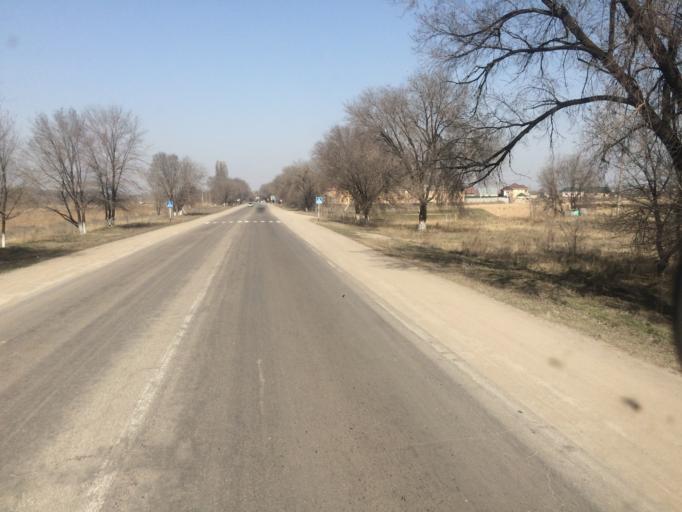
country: KZ
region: Almaty Oblysy
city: Burunday
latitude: 43.2967
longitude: 76.6729
